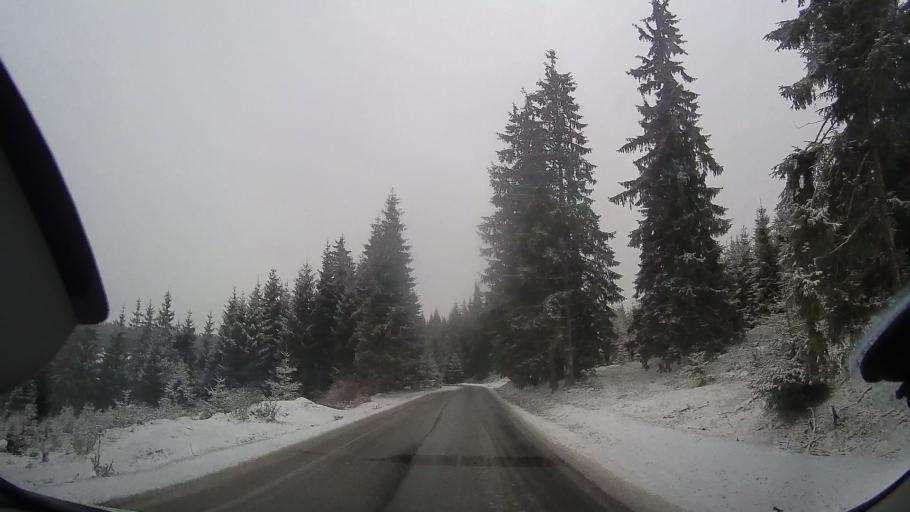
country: RO
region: Cluj
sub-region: Comuna Belis
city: Belis
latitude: 46.6444
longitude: 23.0672
